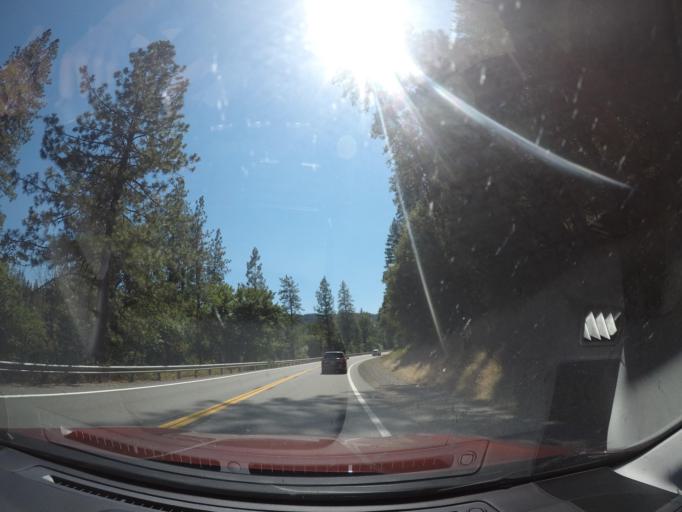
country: US
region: California
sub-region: Shasta County
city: Bella Vista
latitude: 40.7553
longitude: -122.0191
